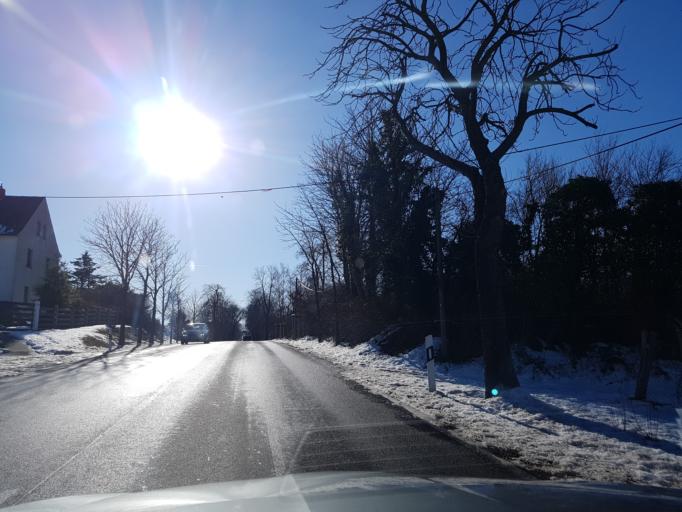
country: DE
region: Saxony
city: Moritzburg
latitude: 51.1295
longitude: 13.6859
